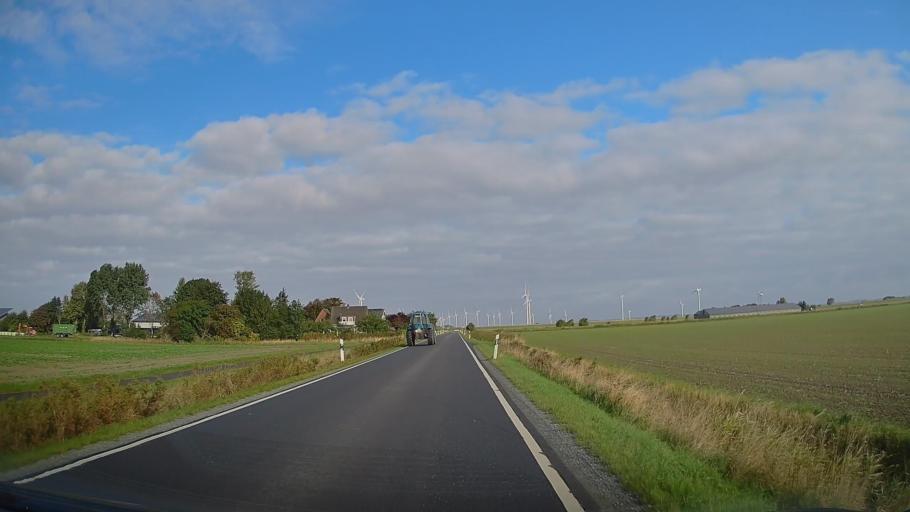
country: DE
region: Schleswig-Holstein
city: Reussenkoge
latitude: 54.5823
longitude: 8.9252
